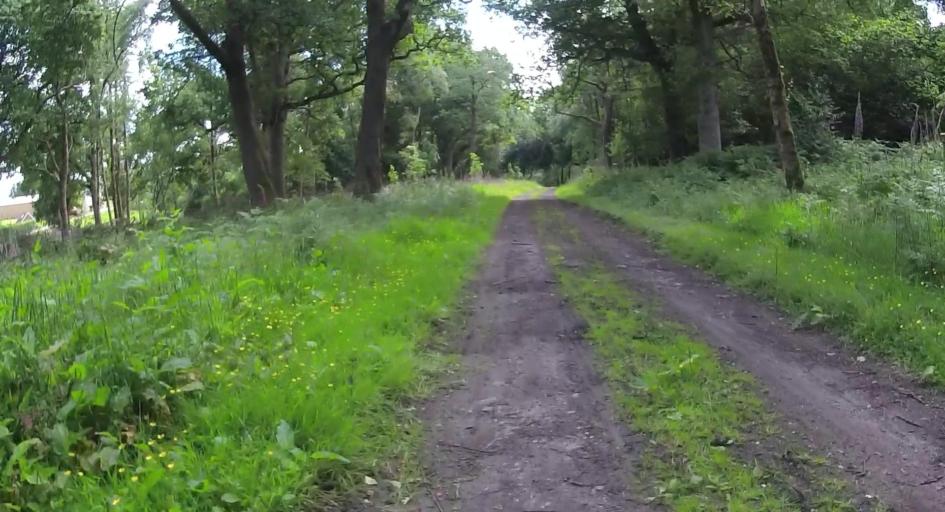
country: GB
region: England
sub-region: Hampshire
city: Basingstoke
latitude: 51.1905
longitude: -1.1659
